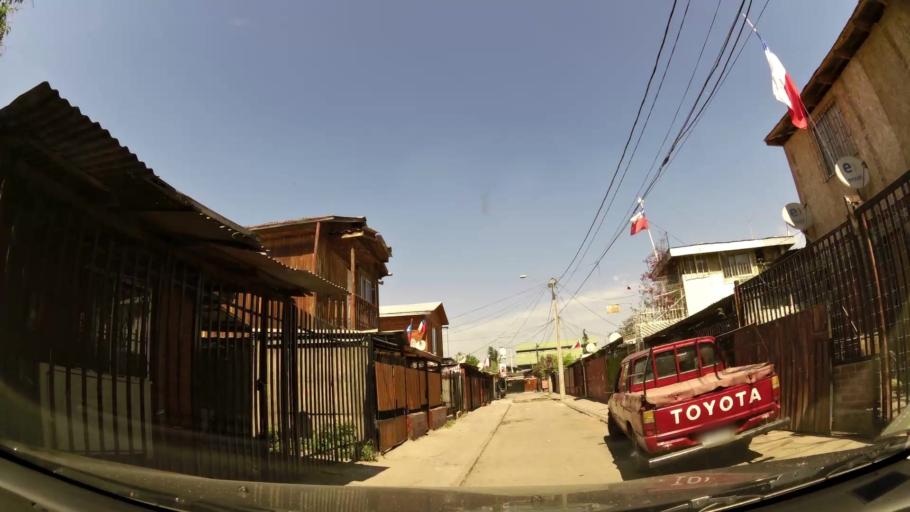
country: CL
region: Santiago Metropolitan
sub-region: Provincia de Santiago
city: La Pintana
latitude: -33.5917
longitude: -70.6273
